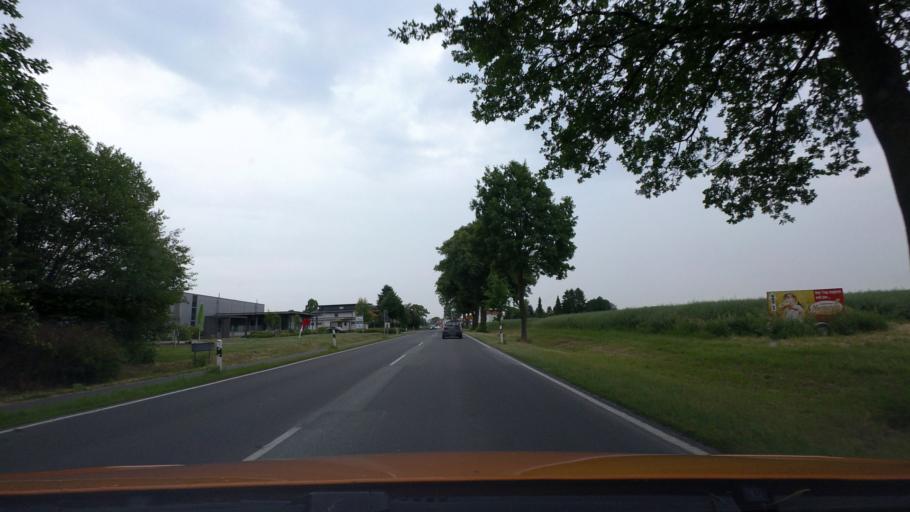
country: DE
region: Lower Saxony
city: Asendorf
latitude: 52.7651
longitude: 9.0114
